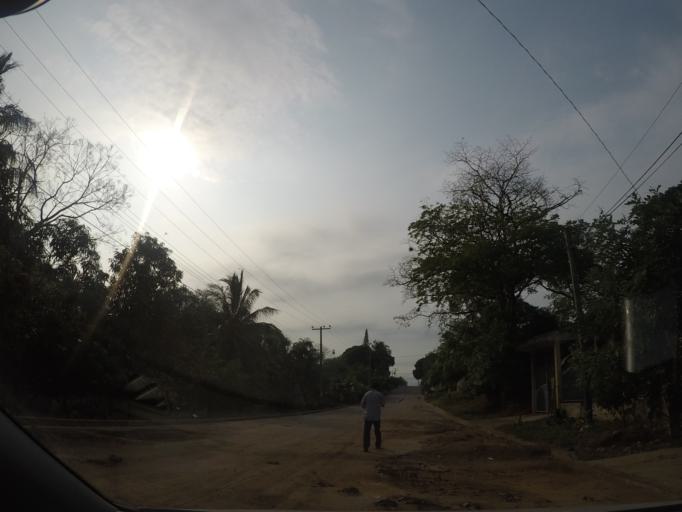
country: MX
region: Oaxaca
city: Colonia Rincon Viejo
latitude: 16.8858
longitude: -95.0457
